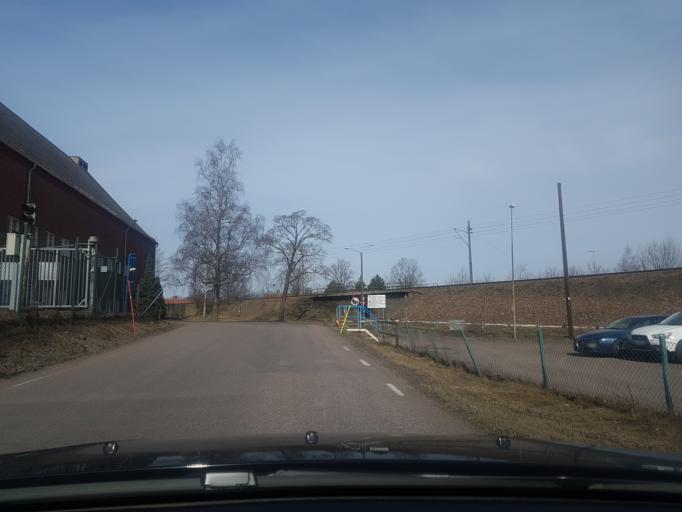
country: SE
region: Dalarna
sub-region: Borlange Kommun
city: Borlaenge
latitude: 60.4979
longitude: 15.4590
